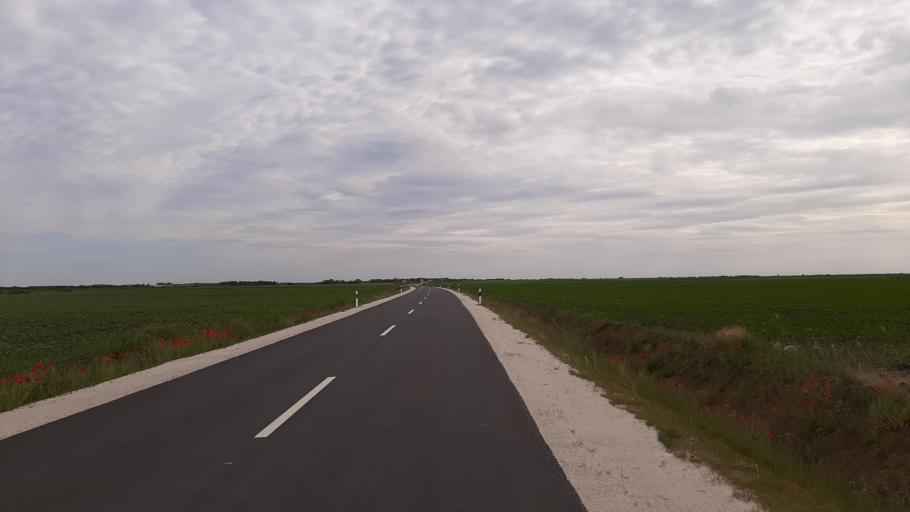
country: RO
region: Timis
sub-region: Comuna Beba Veche
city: Beba Veche
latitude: 46.1355
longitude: 20.2712
